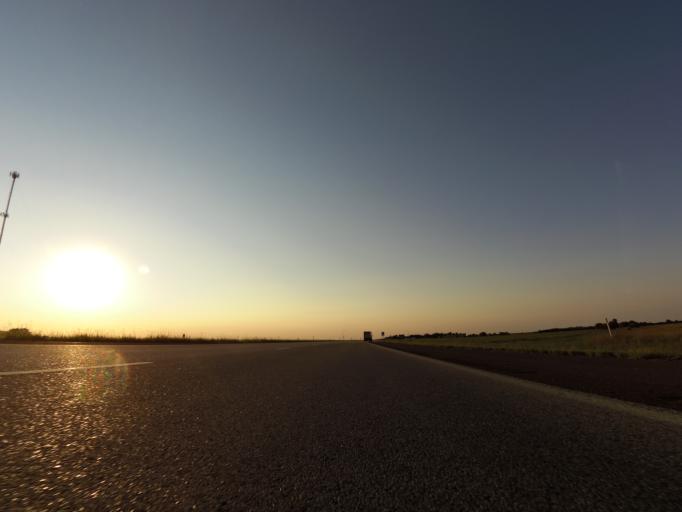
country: US
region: Kansas
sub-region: Reno County
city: South Hutchinson
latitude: 37.9707
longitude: -97.9353
